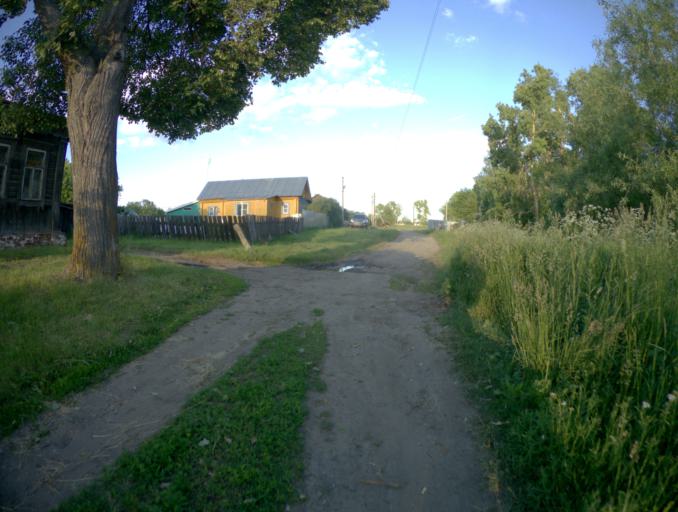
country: RU
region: Vladimir
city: Stavrovo
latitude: 56.2926
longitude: 39.9507
